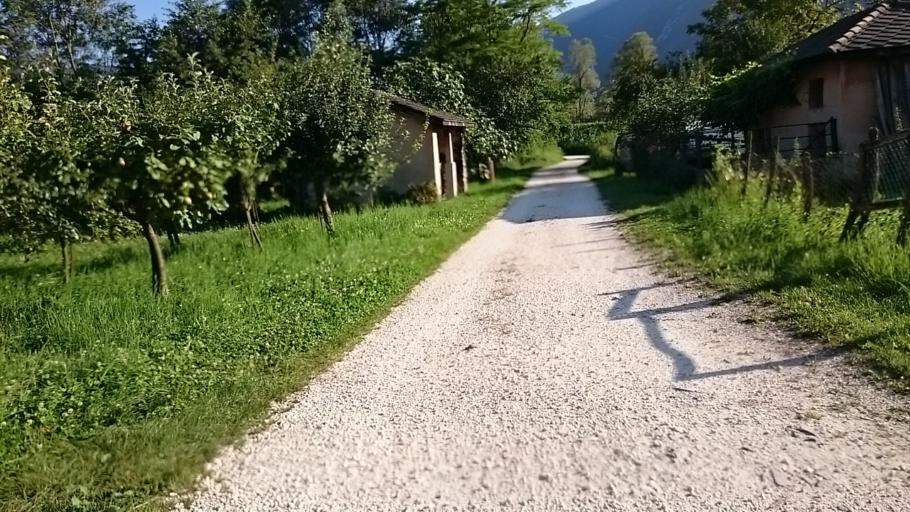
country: IT
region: Veneto
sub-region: Provincia di Belluno
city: Farra d'Alpago
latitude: 46.1275
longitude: 12.3362
